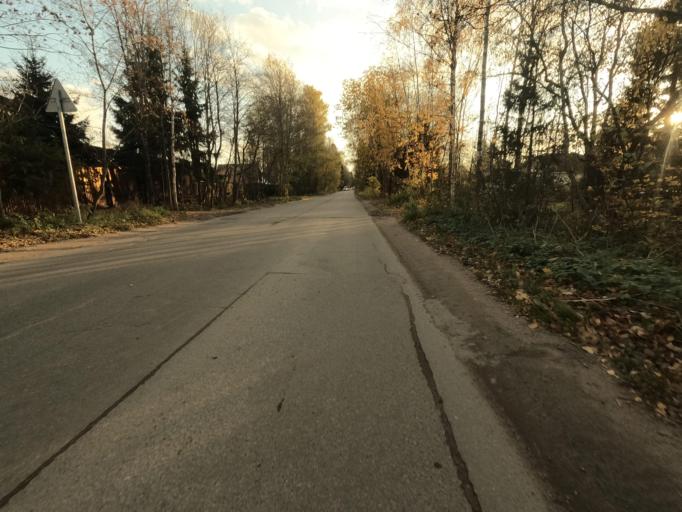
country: RU
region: St.-Petersburg
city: Beloostrov
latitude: 60.1702
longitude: 30.0128
